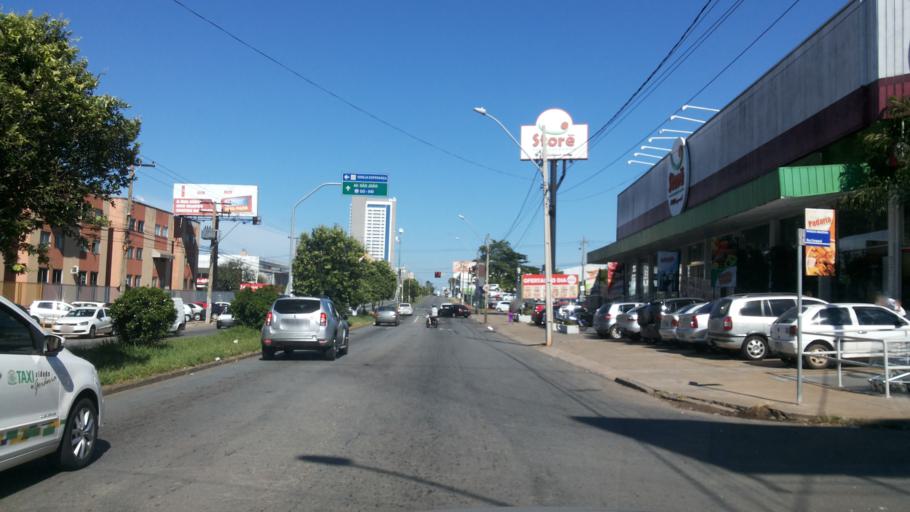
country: BR
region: Goias
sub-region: Goiania
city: Goiania
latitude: -16.7392
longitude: -49.2716
